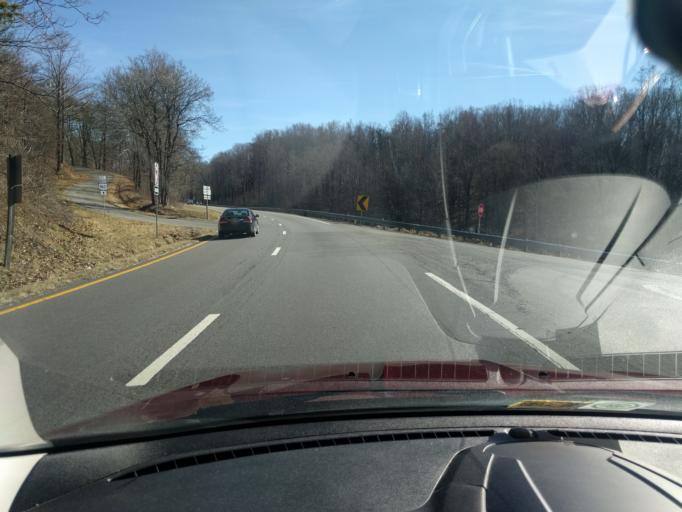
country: US
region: Virginia
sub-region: Botetourt County
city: Blue Ridge
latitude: 37.3652
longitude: -79.6930
